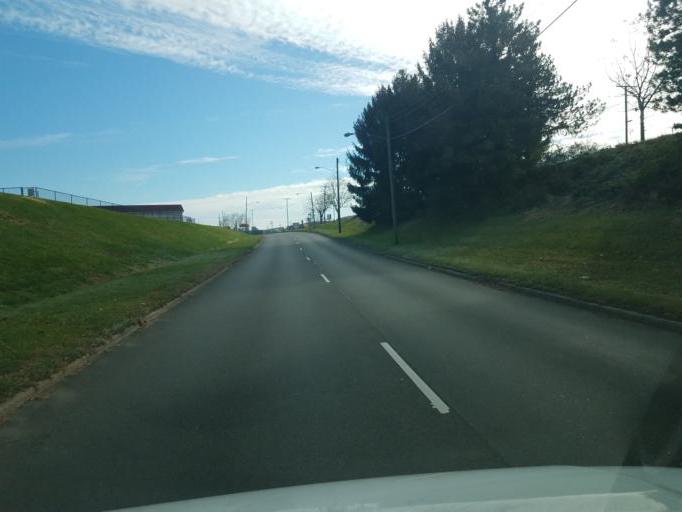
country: US
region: Ohio
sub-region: Scioto County
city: Portsmouth
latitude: 38.7395
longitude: -82.9889
